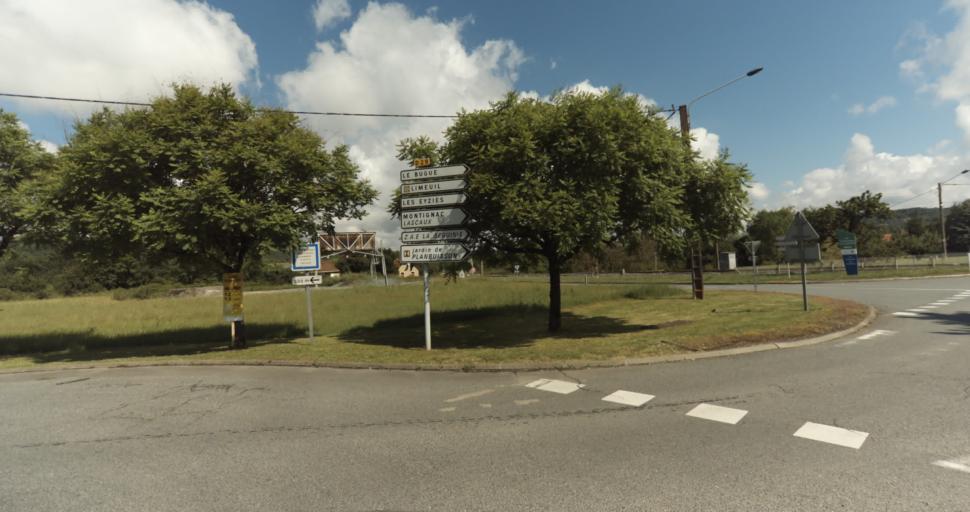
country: FR
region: Aquitaine
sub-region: Departement de la Dordogne
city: Le Bugue
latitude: 44.8483
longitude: 0.9018
